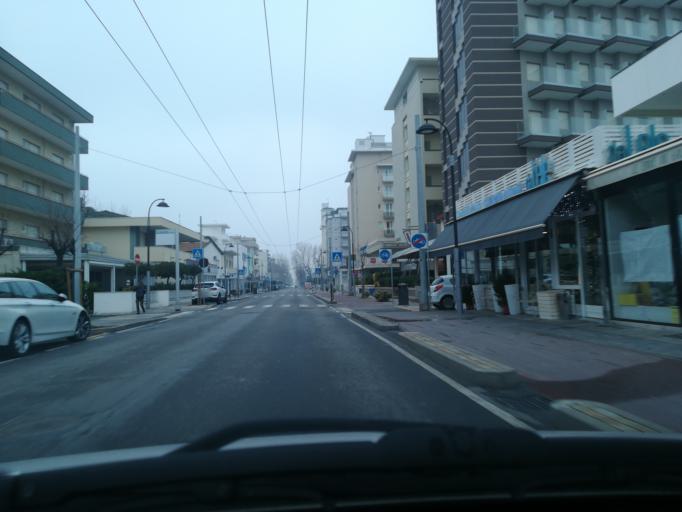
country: IT
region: Emilia-Romagna
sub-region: Provincia di Rimini
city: Riccione
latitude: 44.0140
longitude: 12.6449
